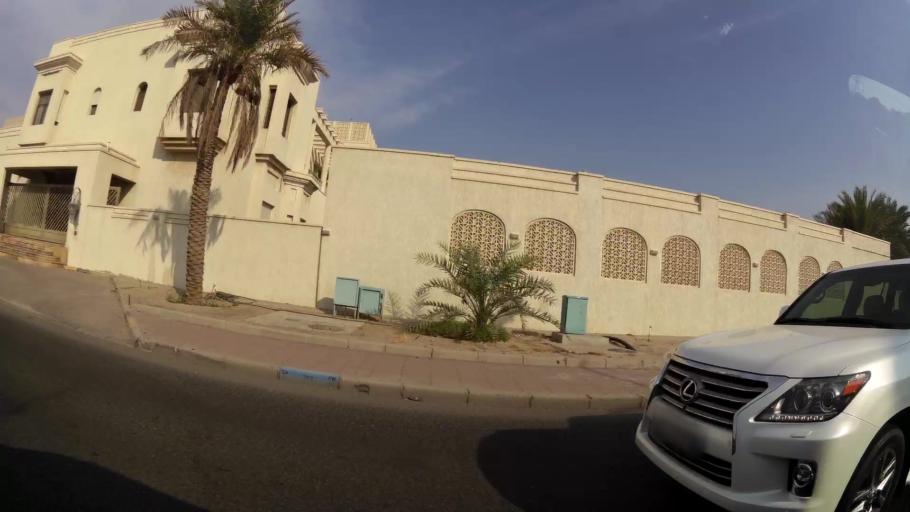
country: KW
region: Al Farwaniyah
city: Janub as Surrah
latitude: 29.3059
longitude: 47.9893
